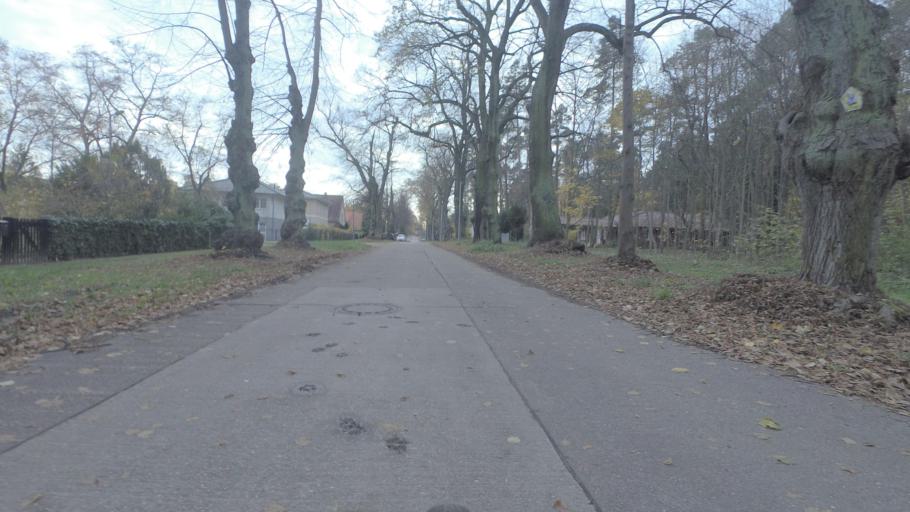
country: DE
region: Brandenburg
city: Rangsdorf
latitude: 52.3006
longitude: 13.4226
